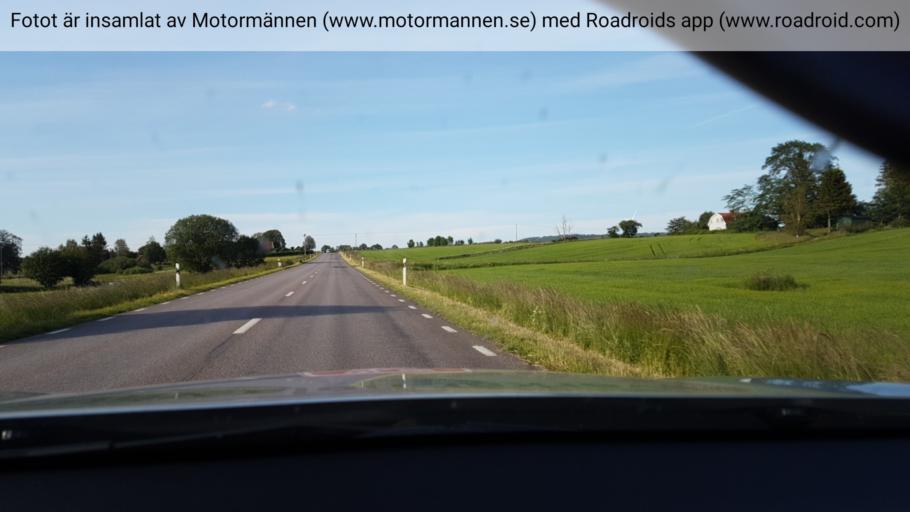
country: SE
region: Vaestra Goetaland
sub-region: Falkopings Kommun
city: Falkoeping
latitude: 58.1026
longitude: 13.5324
